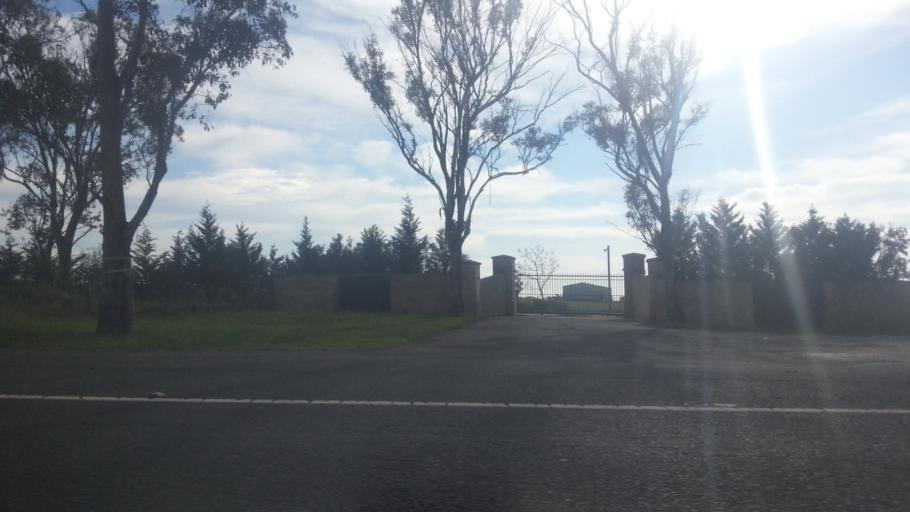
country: AU
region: New South Wales
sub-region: Liverpool
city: Luddenham
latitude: -33.8523
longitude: 150.6927
